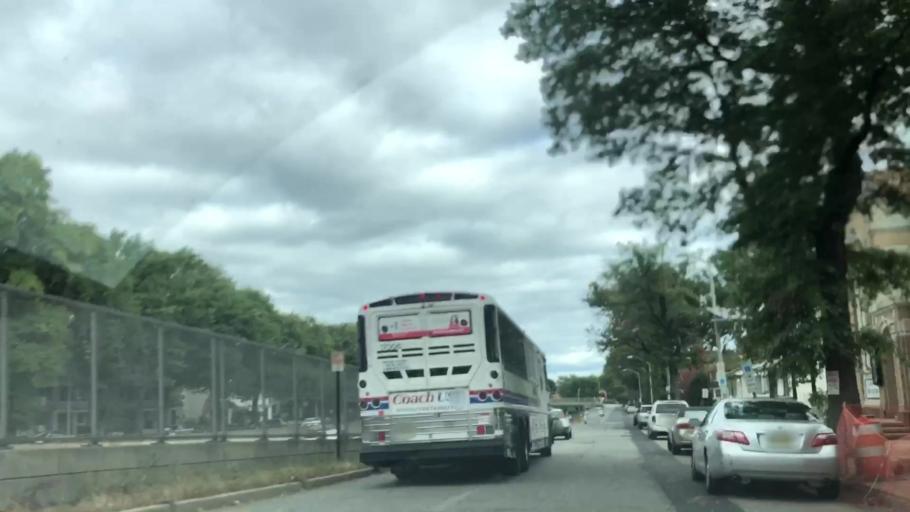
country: US
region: New Jersey
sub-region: Essex County
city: East Orange
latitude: 40.7630
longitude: -74.2059
